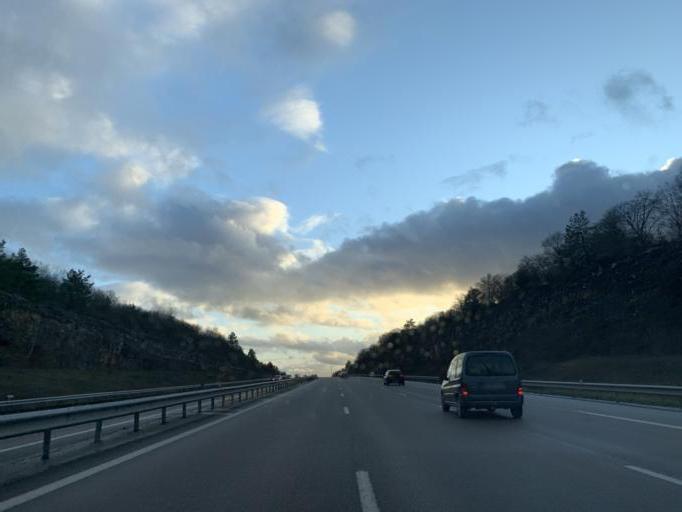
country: FR
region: Bourgogne
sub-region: Departement de la Cote-d'Or
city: Selongey
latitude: 47.6776
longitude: 5.1769
